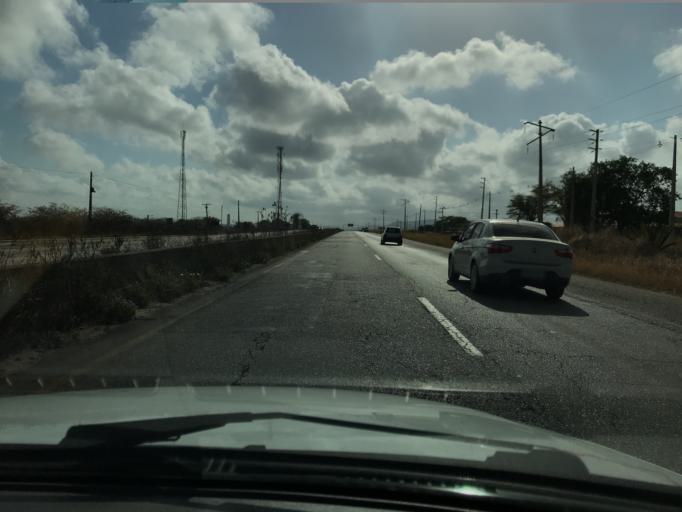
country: BR
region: Pernambuco
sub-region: Gravata
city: Gravata
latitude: -8.2172
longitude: -35.6538
